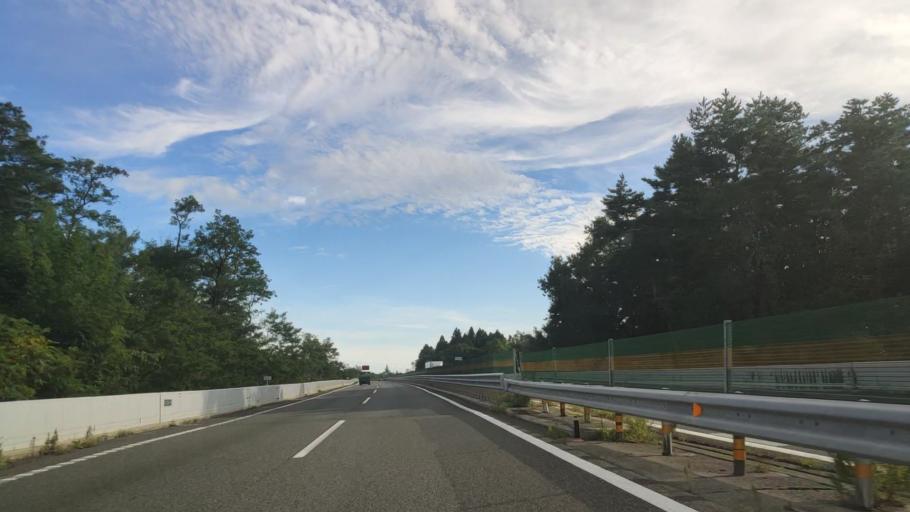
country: JP
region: Nagano
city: Ina
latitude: 35.7499
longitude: 137.9118
